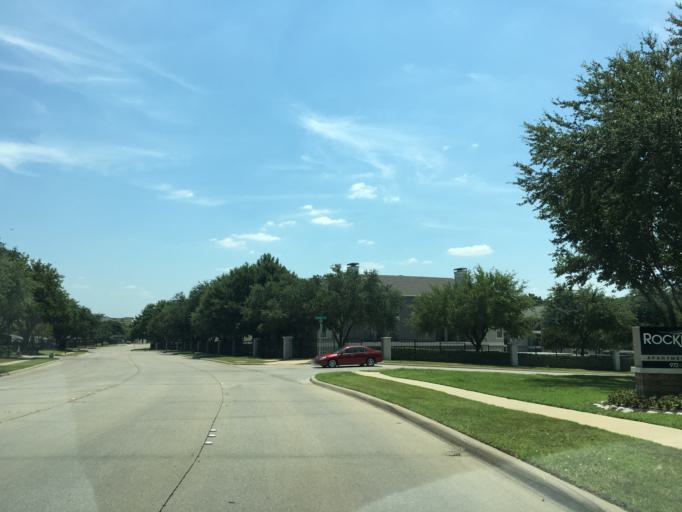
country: US
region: Texas
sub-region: Denton County
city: Lewisville
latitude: 33.0111
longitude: -96.9856
